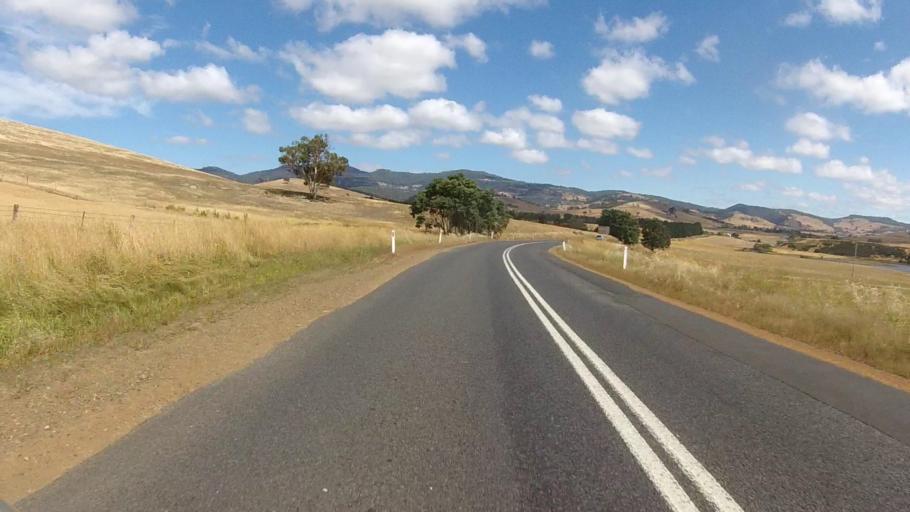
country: AU
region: Tasmania
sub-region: Brighton
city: Bridgewater
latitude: -42.5556
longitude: 147.3859
